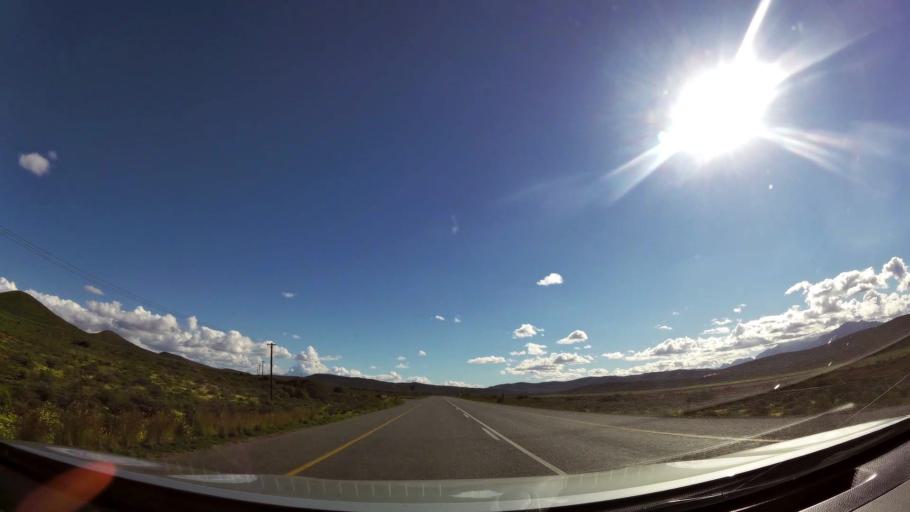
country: ZA
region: Western Cape
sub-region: Cape Winelands District Municipality
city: Worcester
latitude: -33.7524
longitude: 19.7242
